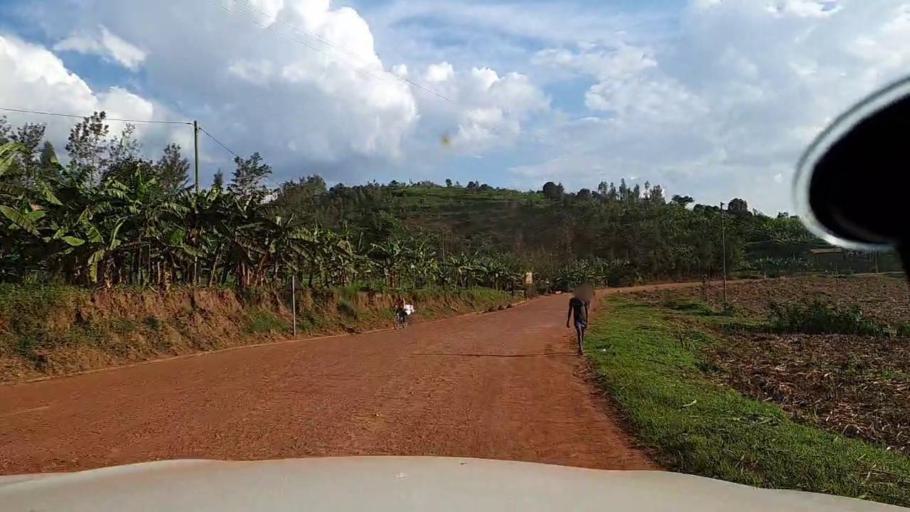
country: RW
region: Kigali
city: Kigali
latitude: -1.9181
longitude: 29.9905
